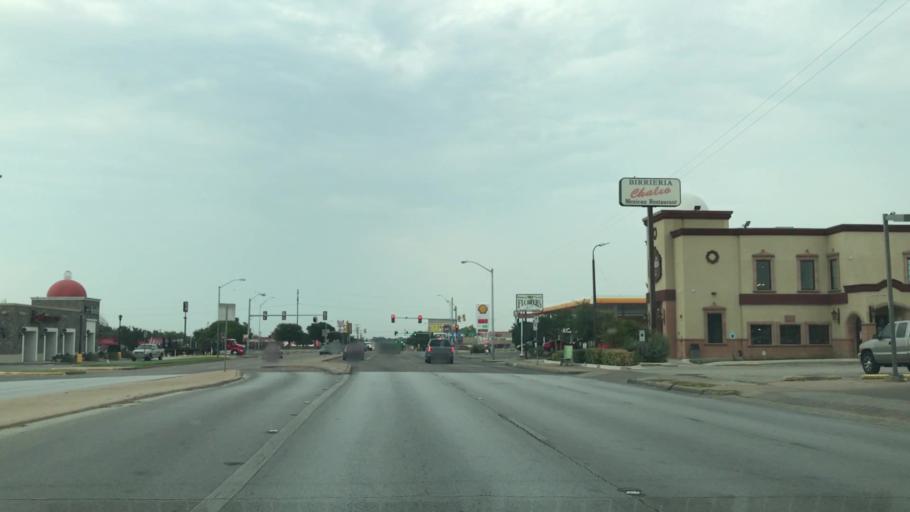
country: US
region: Texas
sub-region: Tarrant County
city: Edgecliff Village
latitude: 32.6843
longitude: -97.3231
